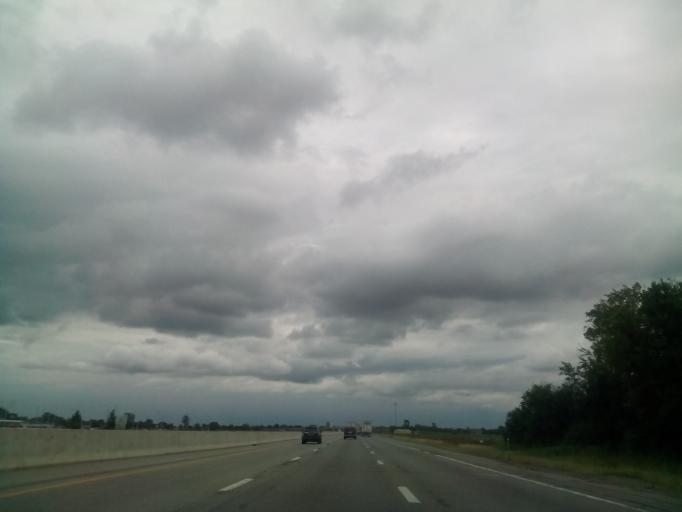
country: US
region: Ohio
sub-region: Wood County
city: Rossford
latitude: 41.5518
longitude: -83.5477
